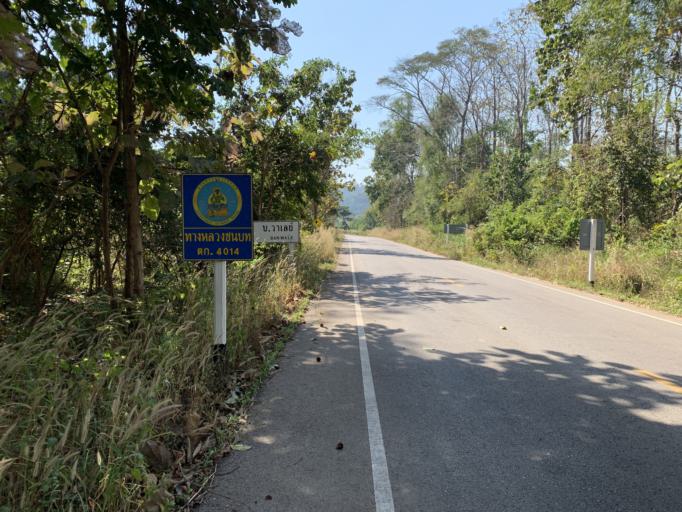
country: TH
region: Tak
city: Phop Phra
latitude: 16.5137
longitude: 98.6386
